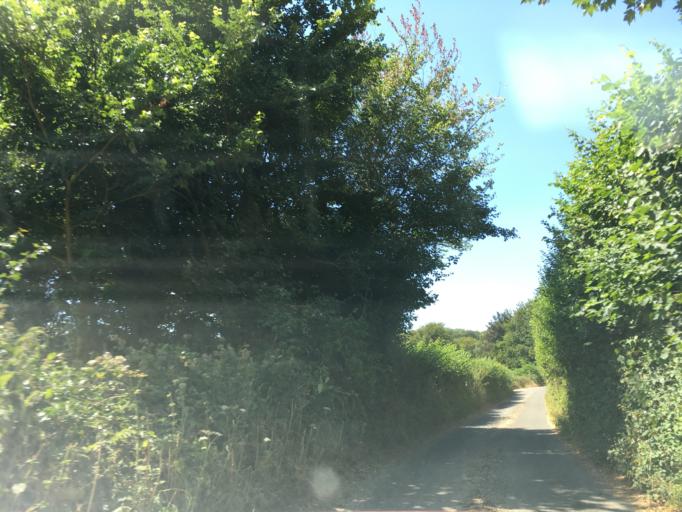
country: GB
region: England
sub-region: Gloucestershire
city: Painswick
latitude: 51.7852
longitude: -2.2143
